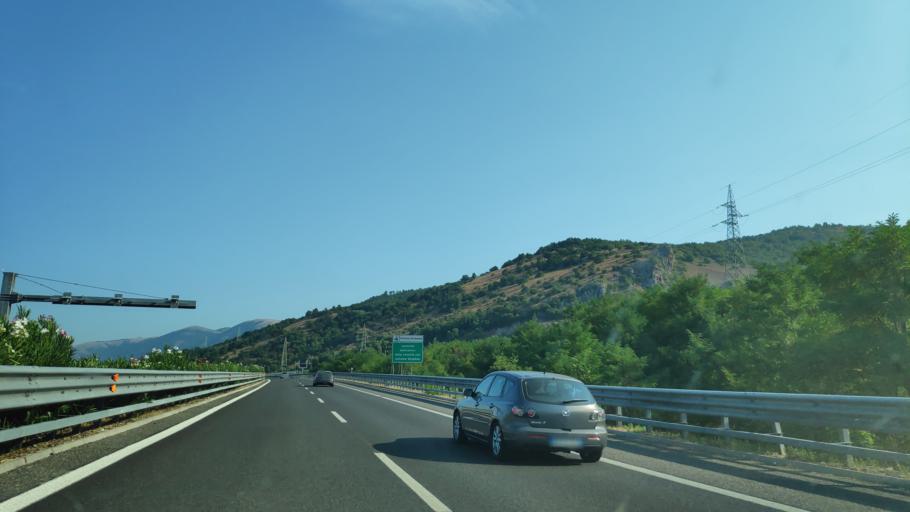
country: IT
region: Campania
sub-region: Provincia di Salerno
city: Atena Lucana
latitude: 40.4555
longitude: 15.5433
